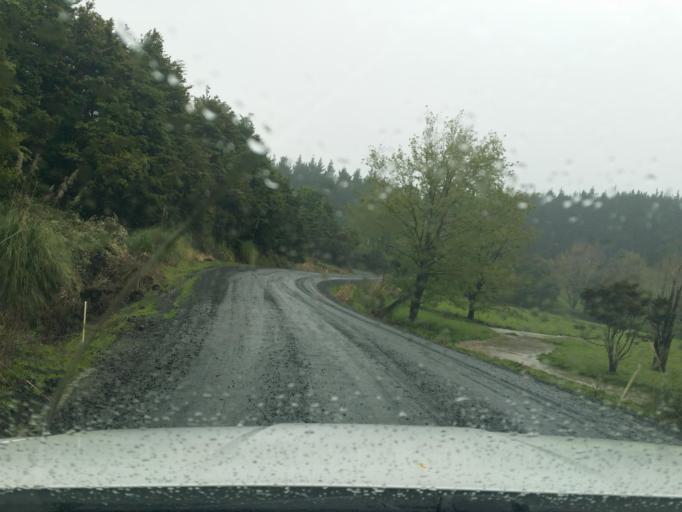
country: NZ
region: Northland
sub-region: Kaipara District
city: Dargaville
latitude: -35.7917
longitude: 173.9743
